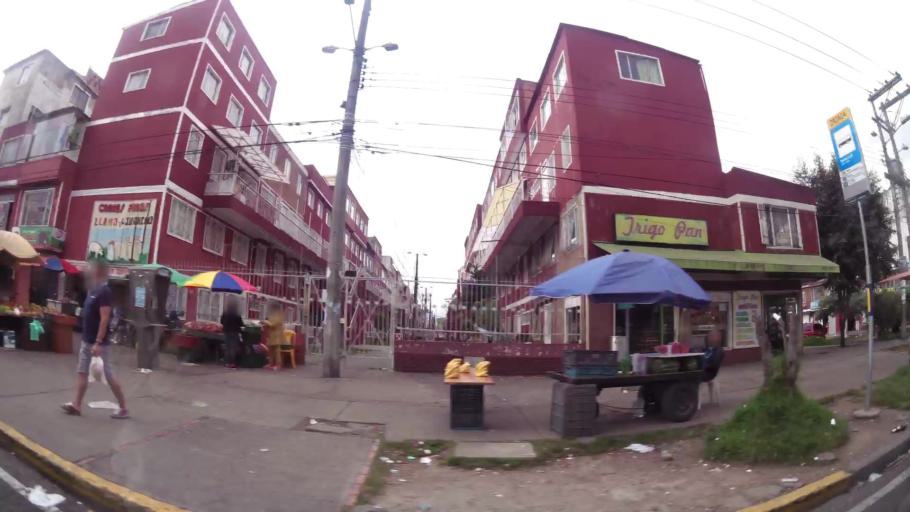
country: CO
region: Bogota D.C.
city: Barrio San Luis
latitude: 4.7123
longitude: -74.1035
